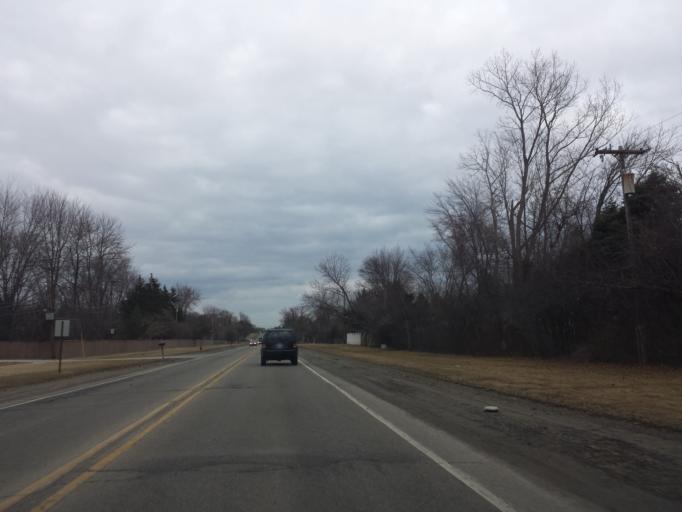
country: US
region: Michigan
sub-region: Oakland County
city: Beverly Hills
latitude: 42.5167
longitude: -83.2385
